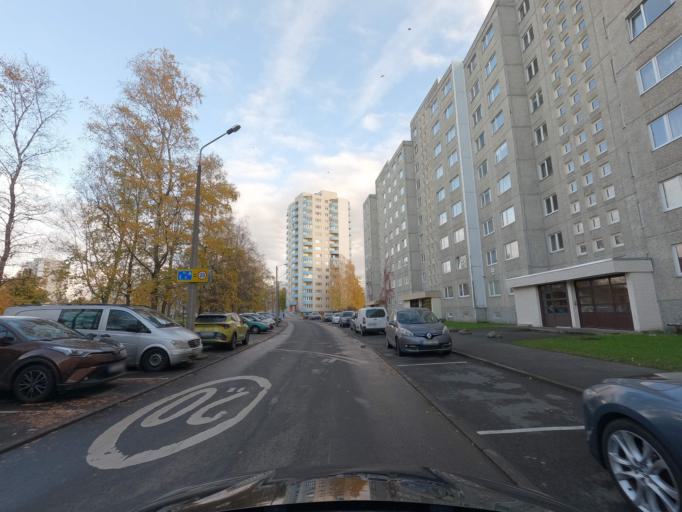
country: EE
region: Harju
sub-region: Saue vald
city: Laagri
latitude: 59.4127
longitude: 24.6451
